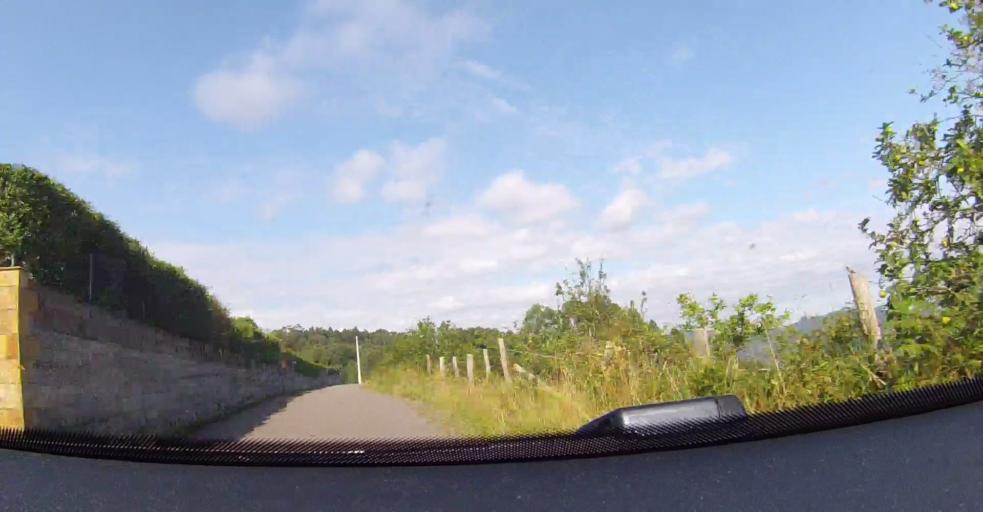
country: ES
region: Asturias
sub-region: Province of Asturias
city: Villaviciosa
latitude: 43.4861
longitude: -5.3937
